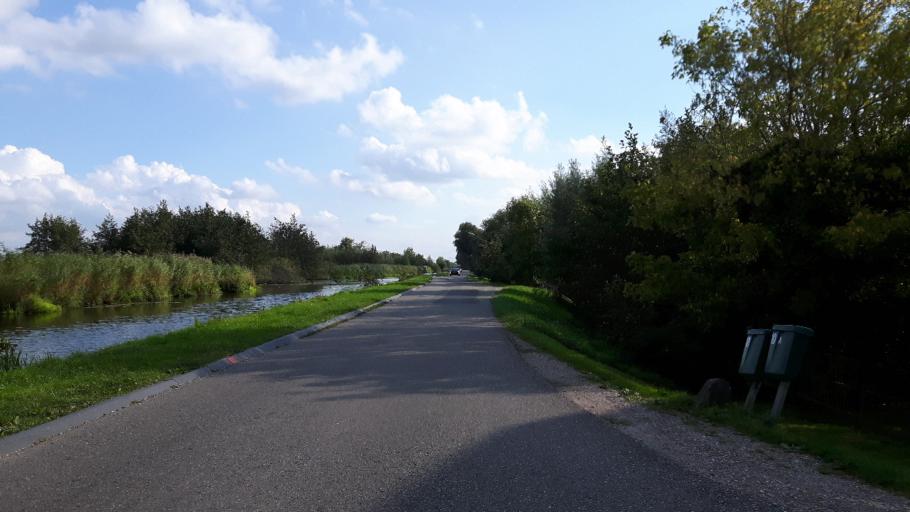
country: NL
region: Utrecht
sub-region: Stichtse Vecht
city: Breukelen
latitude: 52.1418
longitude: 4.9539
